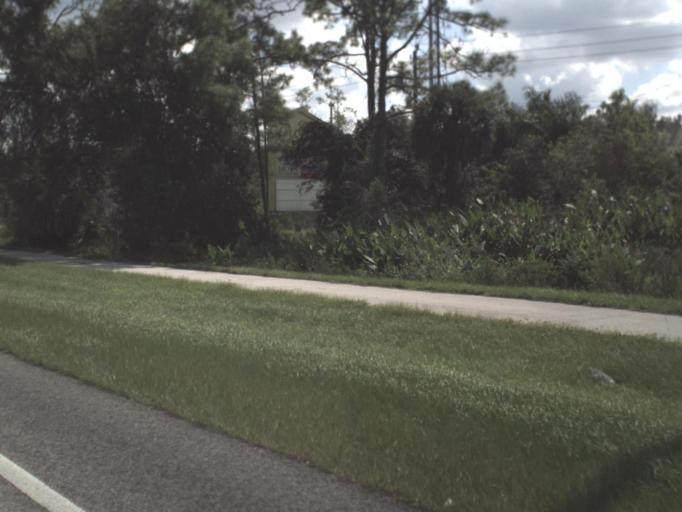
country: US
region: Florida
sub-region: Lee County
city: Fort Myers
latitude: 26.6128
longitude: -81.7994
